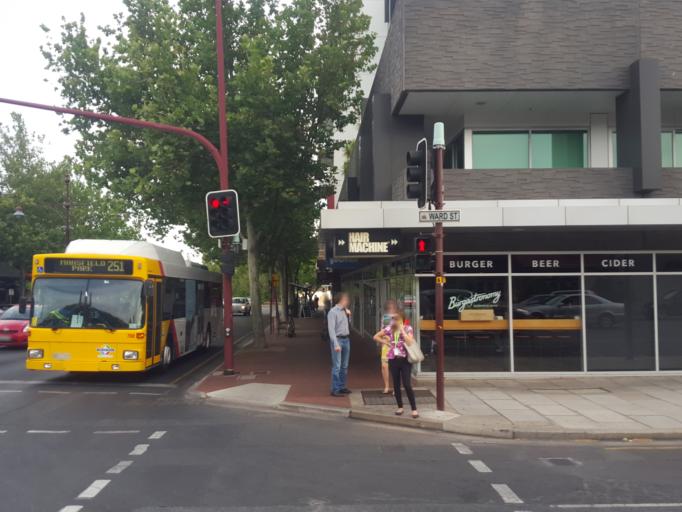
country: AU
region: South Australia
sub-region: Adelaide
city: North Adelaide
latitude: -34.9087
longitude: 138.5967
